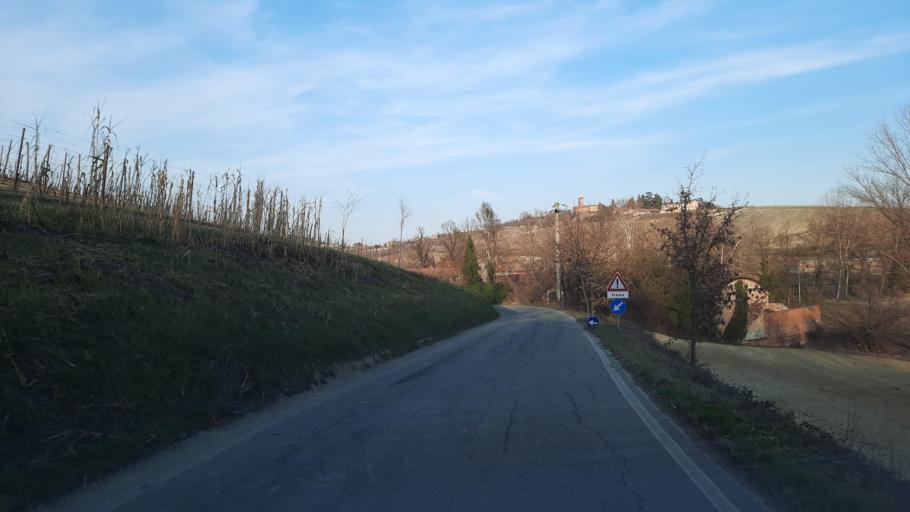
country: IT
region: Piedmont
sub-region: Provincia di Alessandria
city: Cella Monte
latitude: 45.0688
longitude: 8.3997
